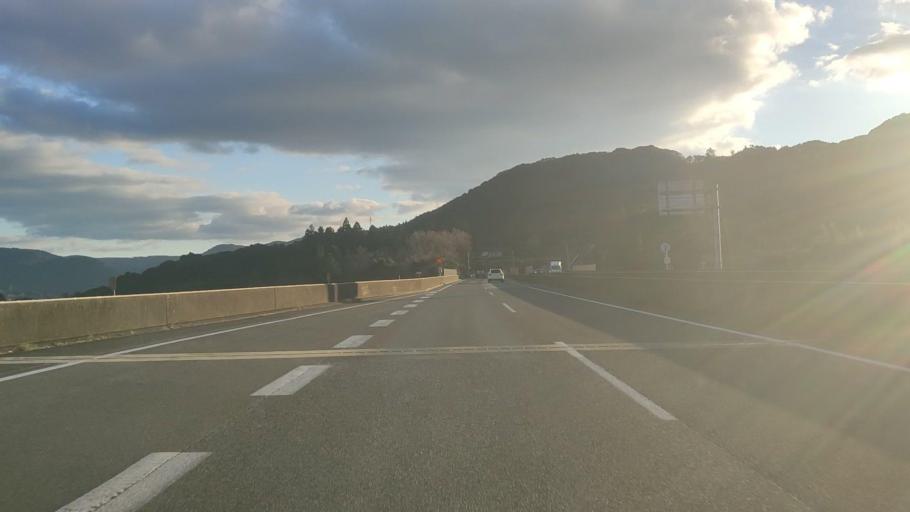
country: JP
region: Saga Prefecture
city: Ureshinomachi-shimojuku
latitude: 33.1098
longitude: 129.9748
